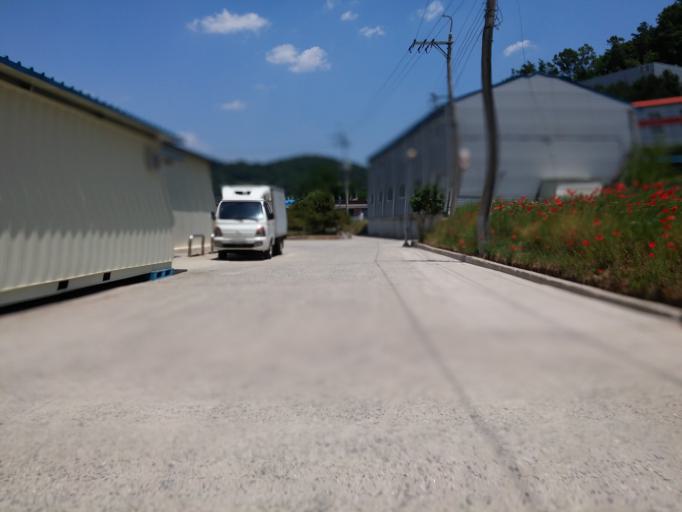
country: KR
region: Chungcheongbuk-do
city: Cheongju-si
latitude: 36.5584
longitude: 127.4372
